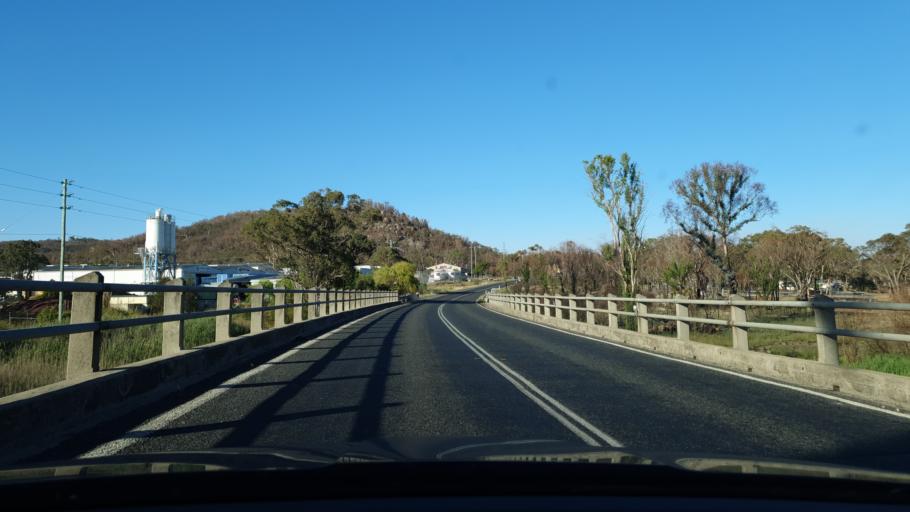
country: AU
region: Queensland
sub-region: Southern Downs
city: Stanthorpe
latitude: -28.6536
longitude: 151.9182
